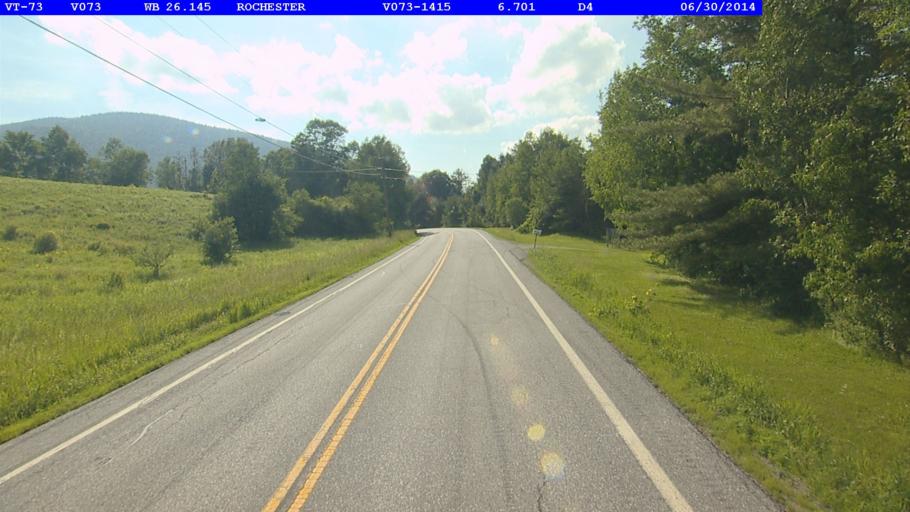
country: US
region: Vermont
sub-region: Orange County
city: Randolph
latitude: 43.8491
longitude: -72.8429
